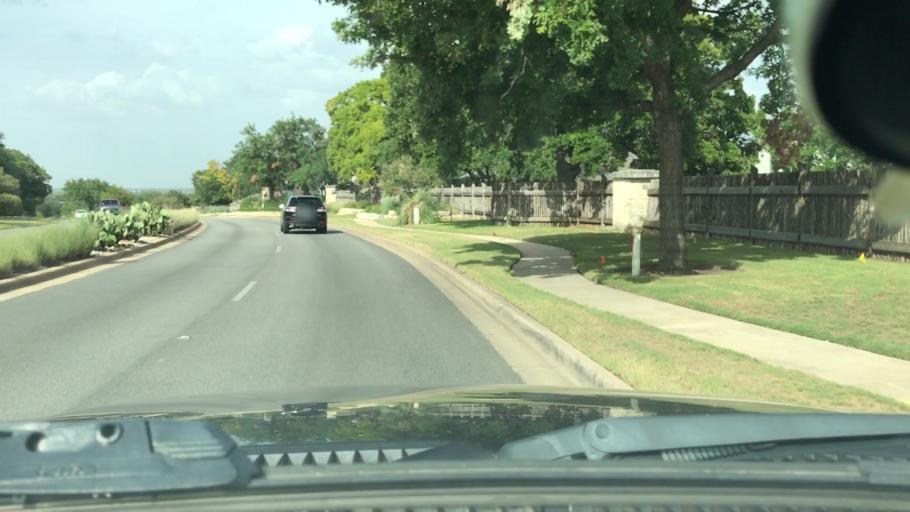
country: US
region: Texas
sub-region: Williamson County
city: Leander
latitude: 30.5470
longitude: -97.8590
